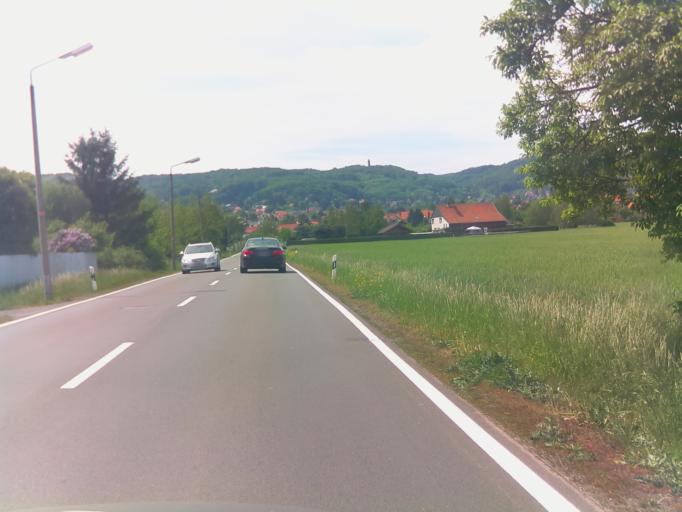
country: DE
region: Saxony-Anhalt
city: Blankenburg
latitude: 51.7949
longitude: 10.9818
